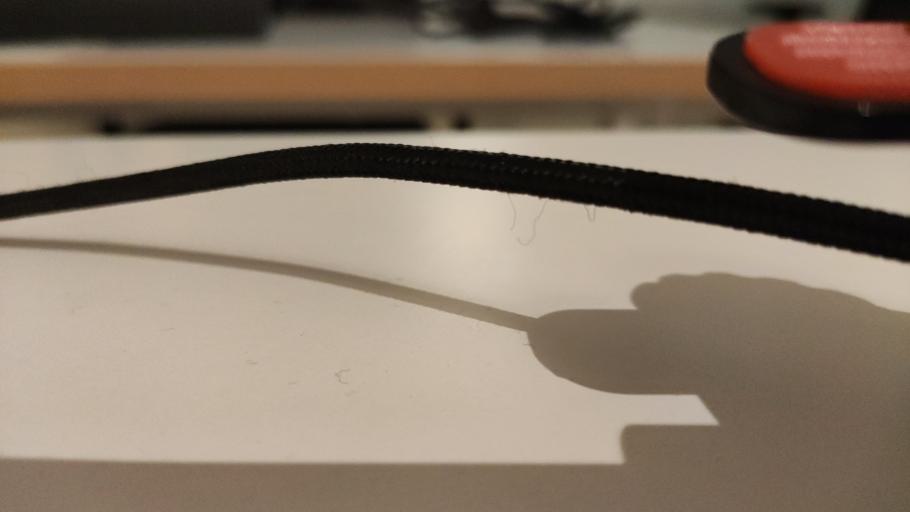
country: RU
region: Moskovskaya
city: Il'inskiy Pogost
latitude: 55.5258
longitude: 38.8721
